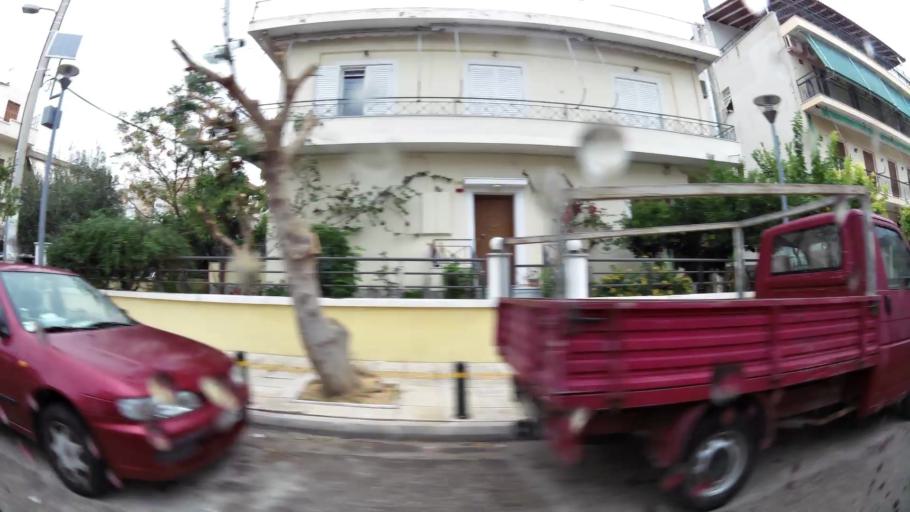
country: GR
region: Attica
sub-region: Nomarchia Athinas
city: Agia Varvara
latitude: 37.9930
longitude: 23.6685
